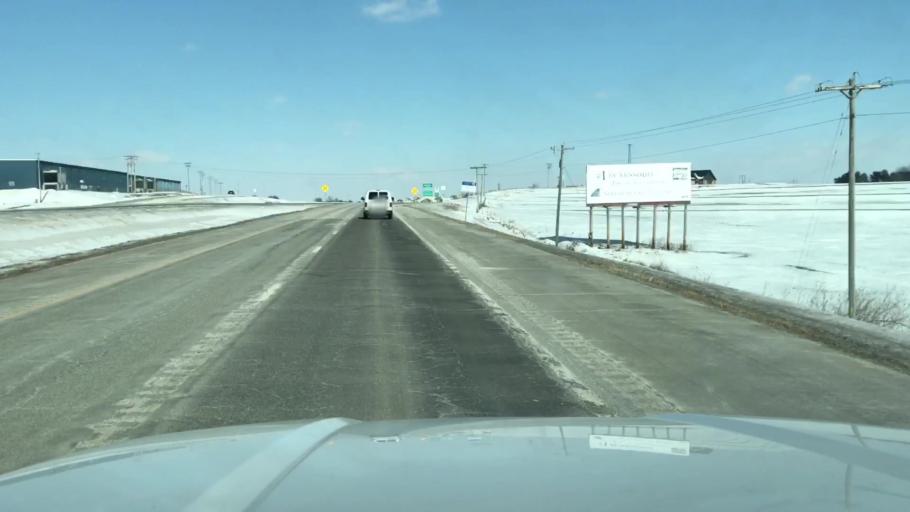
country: US
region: Missouri
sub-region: Nodaway County
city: Maryville
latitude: 40.3086
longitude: -94.8743
